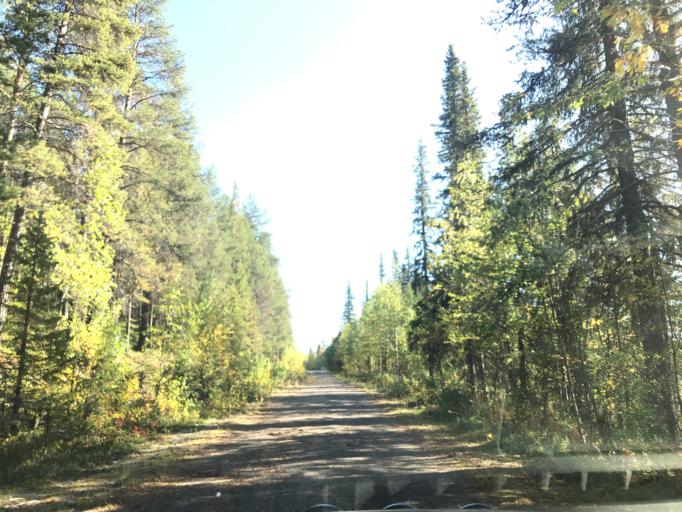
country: SE
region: Norrbotten
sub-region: Gallivare Kommun
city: Malmberget
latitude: 67.6469
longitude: 21.0934
